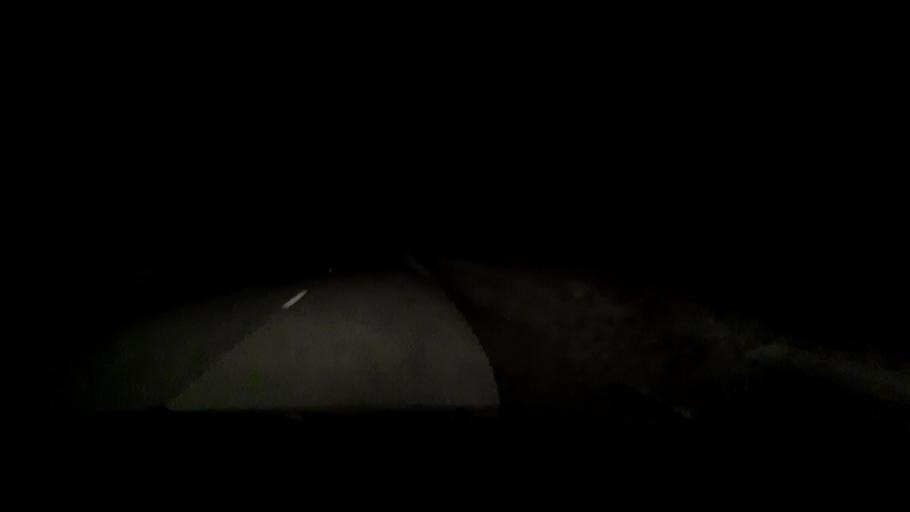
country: RU
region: Nizjnij Novgorod
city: Burevestnik
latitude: 56.1374
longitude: 43.7674
